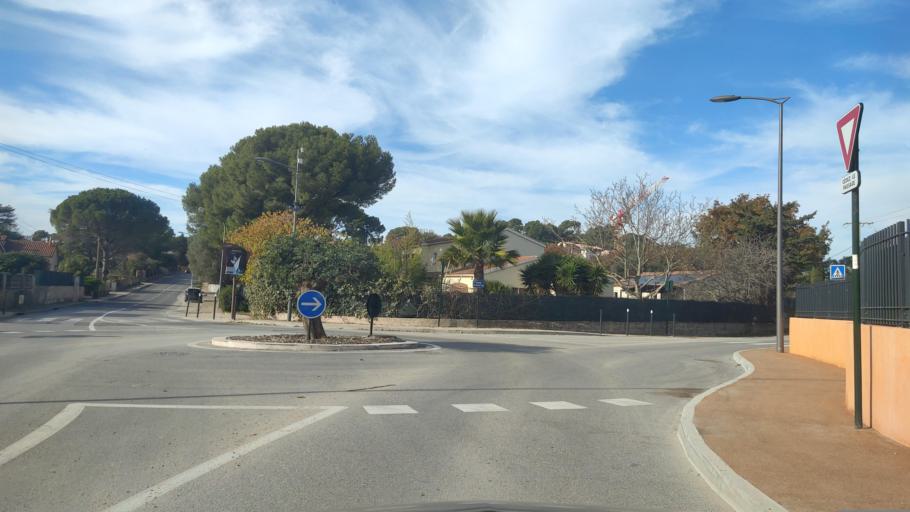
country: FR
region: Provence-Alpes-Cote d'Azur
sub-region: Departement du Var
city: Sanary-sur-Mer
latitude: 43.1270
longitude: 5.8194
